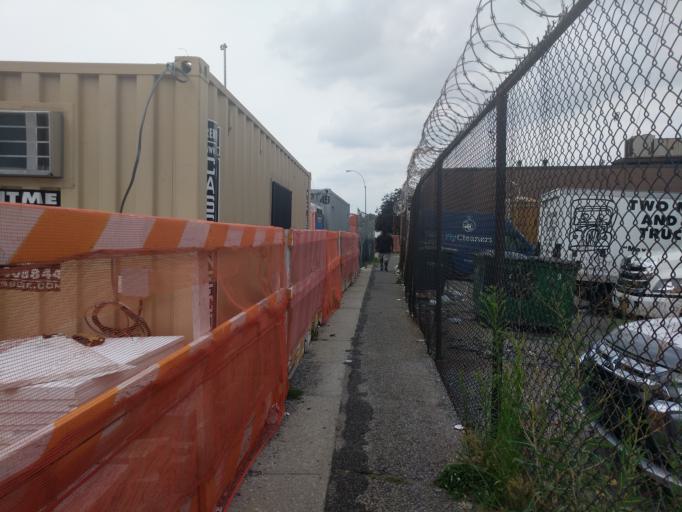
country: US
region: New York
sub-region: Queens County
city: Long Island City
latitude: 40.7538
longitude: -73.9168
